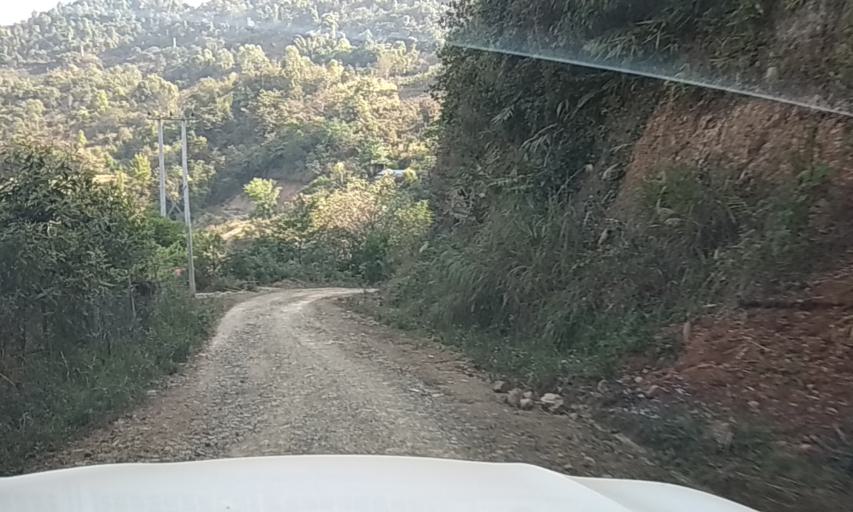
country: LA
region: Phongsali
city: Phongsali
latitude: 21.6877
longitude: 102.1011
